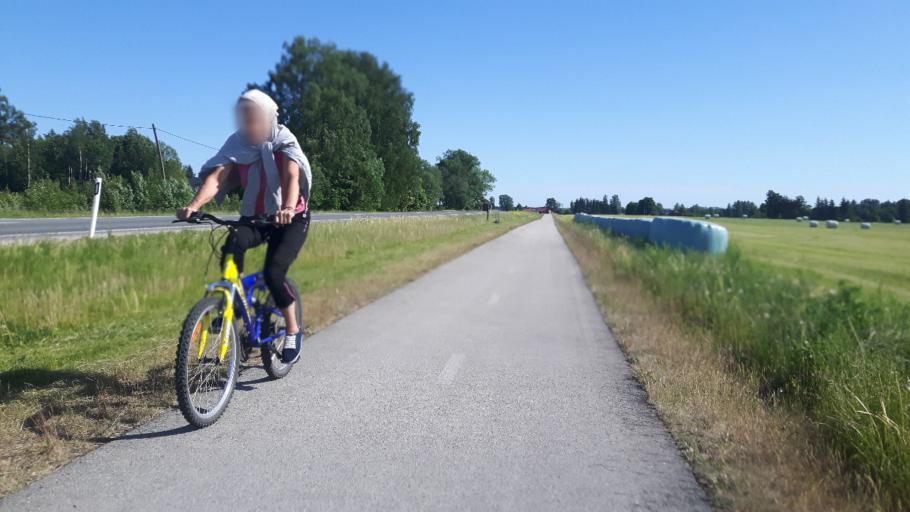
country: EE
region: Raplamaa
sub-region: Kehtna vald
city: Kehtna
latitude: 58.9473
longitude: 24.8764
